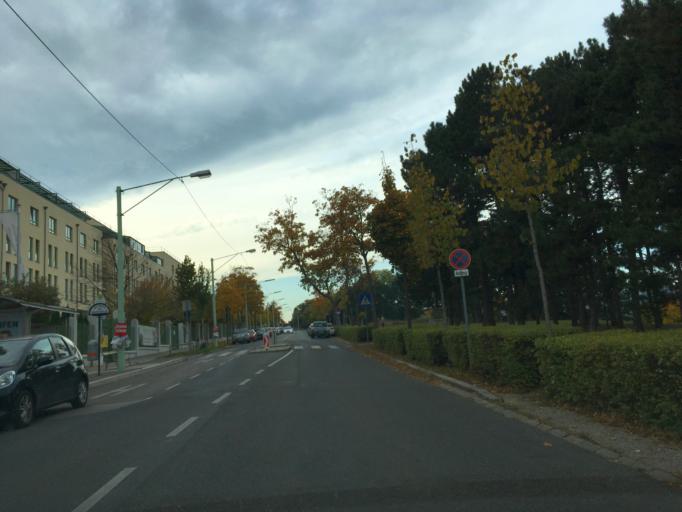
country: AT
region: Vienna
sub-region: Wien Stadt
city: Vienna
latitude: 48.2389
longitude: 16.3332
